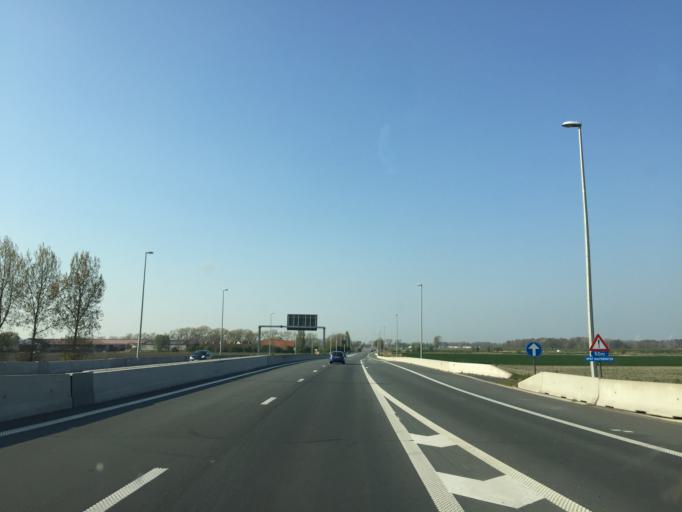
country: BE
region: Flanders
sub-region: Provincie West-Vlaanderen
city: Zuienkerke
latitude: 51.2695
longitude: 3.1970
